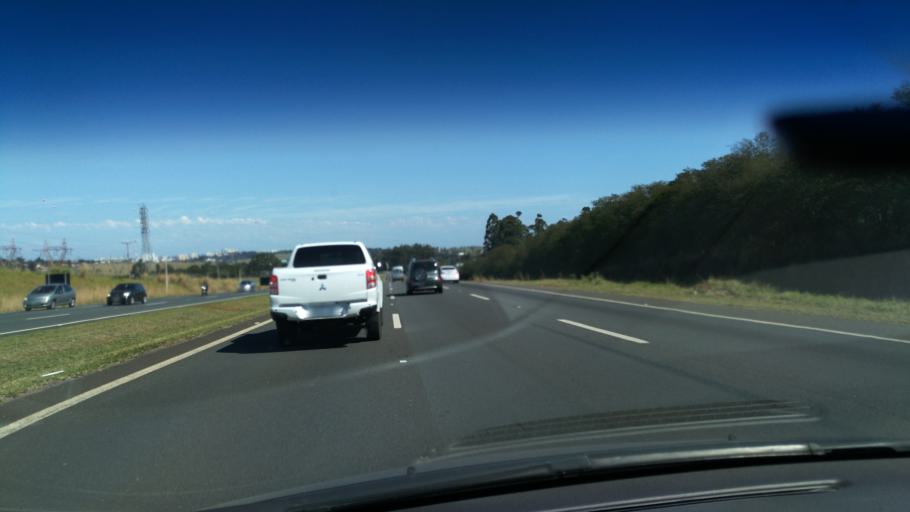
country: BR
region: Sao Paulo
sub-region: Jaguariuna
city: Jaguariuna
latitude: -22.7790
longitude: -47.0245
